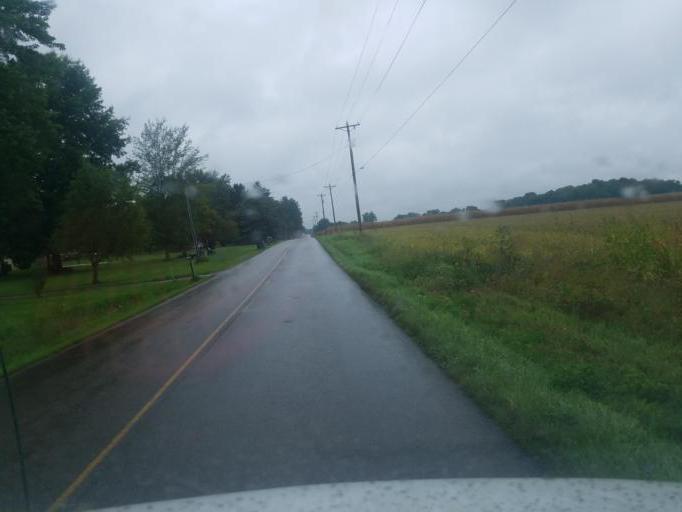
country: US
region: Ohio
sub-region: Medina County
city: Westfield Center
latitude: 40.9738
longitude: -81.9607
